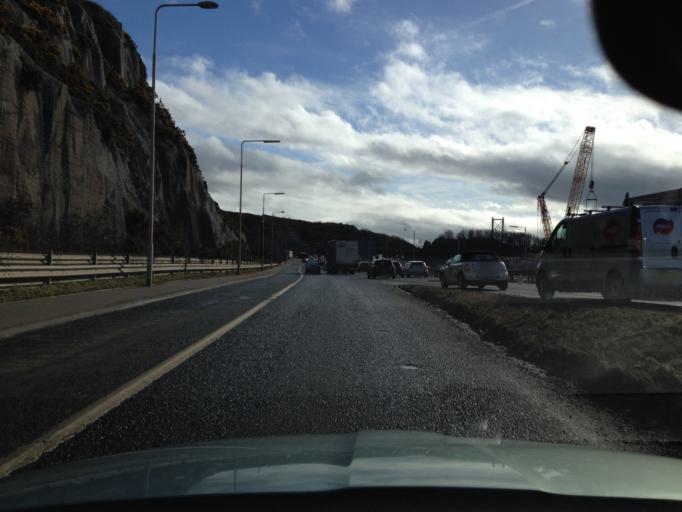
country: GB
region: Scotland
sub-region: Fife
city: Inverkeithing
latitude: 56.0199
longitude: -3.4055
